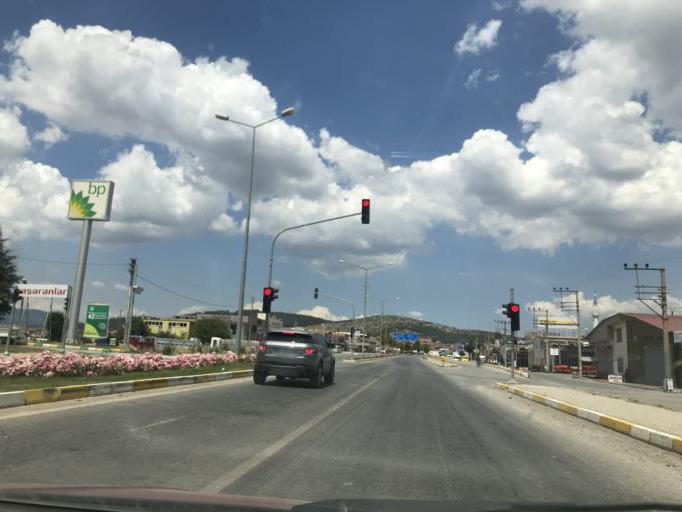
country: TR
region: Denizli
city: Tavas
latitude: 37.5610
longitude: 29.0603
